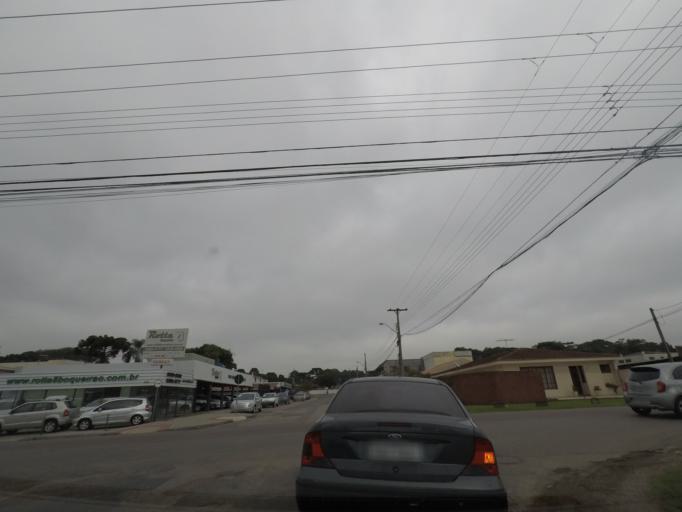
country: BR
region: Parana
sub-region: Sao Jose Dos Pinhais
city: Sao Jose dos Pinhais
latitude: -25.5044
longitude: -49.2347
